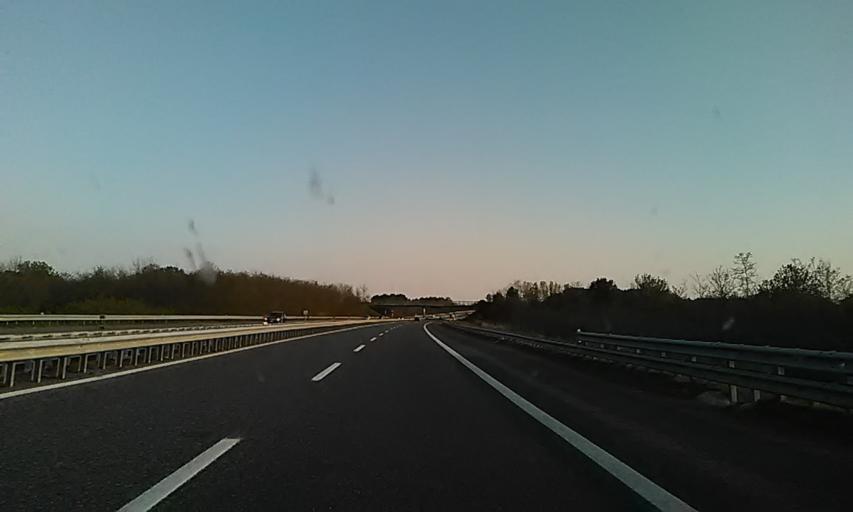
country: IT
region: Piedmont
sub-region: Provincia di Novara
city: Carpignano Sesia
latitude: 45.5370
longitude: 8.4298
